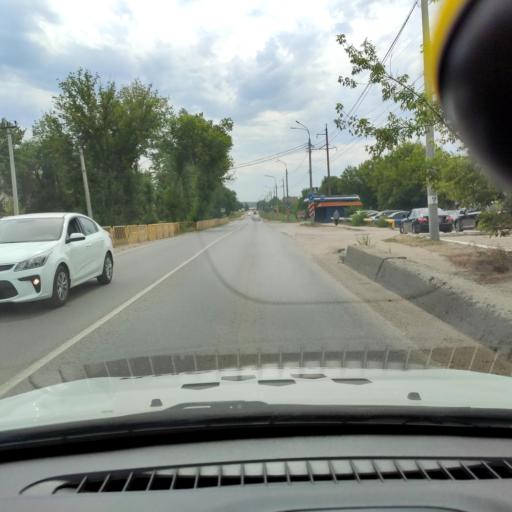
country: RU
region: Samara
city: Zhigulevsk
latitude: 53.4090
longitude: 49.5248
